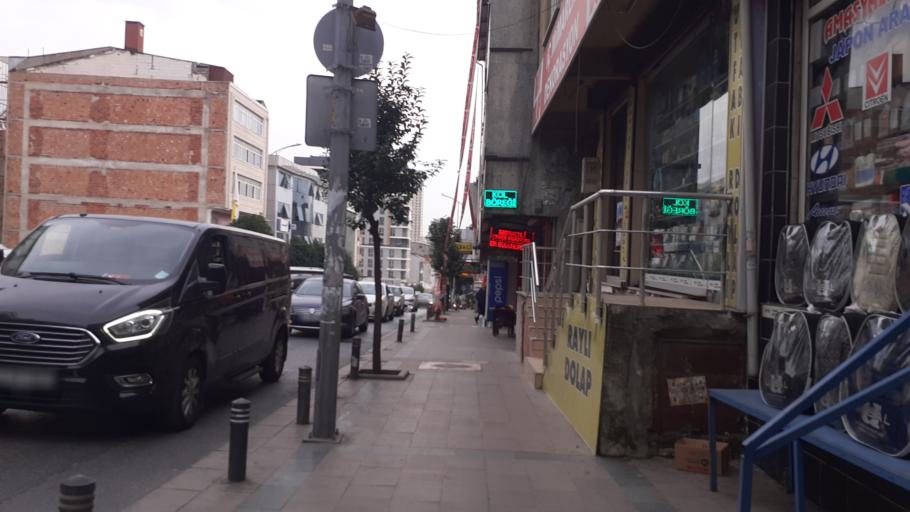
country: TR
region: Istanbul
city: Mahmutbey
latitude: 41.0479
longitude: 28.8018
